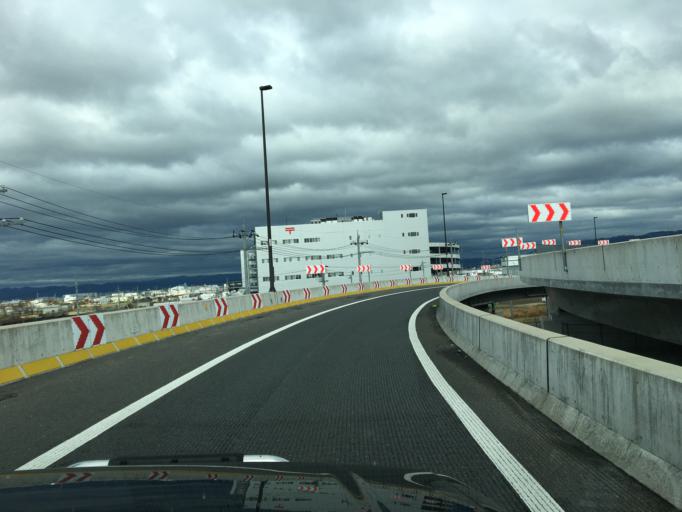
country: JP
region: Kyoto
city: Tanabe
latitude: 34.8540
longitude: 135.7606
